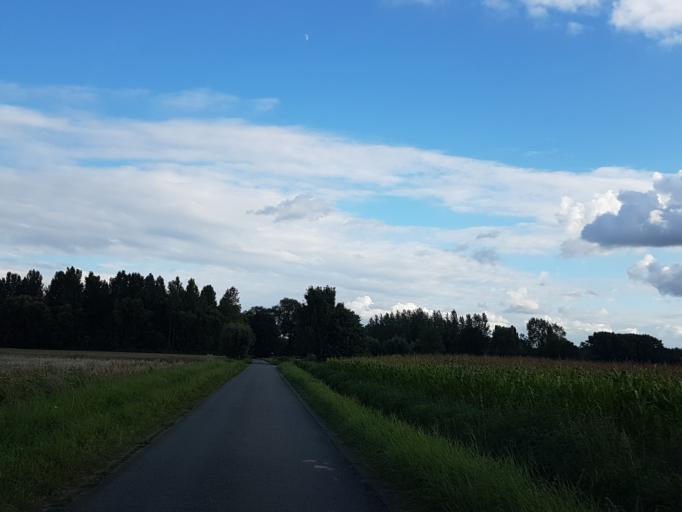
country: BE
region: Flanders
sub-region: Provincie Vlaams-Brabant
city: Kampenhout
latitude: 50.9302
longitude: 4.5947
